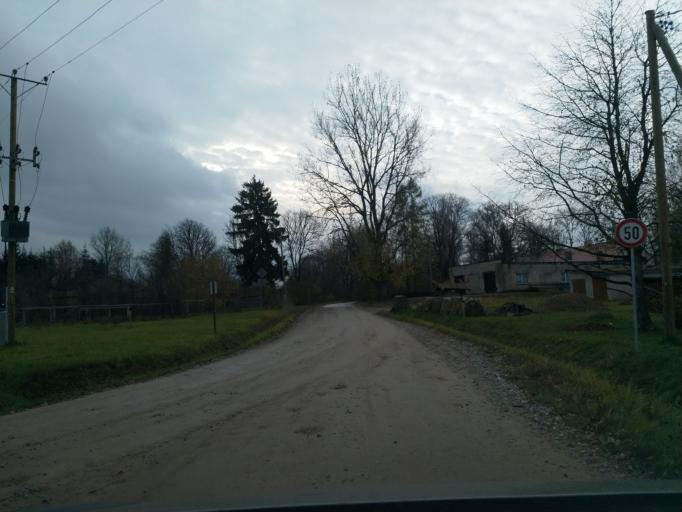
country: LV
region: Kuldigas Rajons
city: Kuldiga
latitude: 56.9828
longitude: 21.9737
